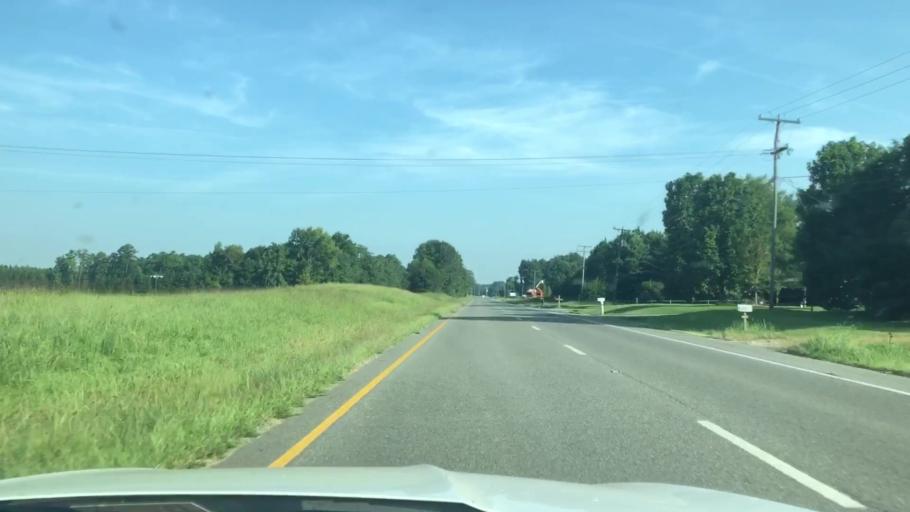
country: US
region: Virginia
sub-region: Middlesex County
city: Saluda
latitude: 37.7064
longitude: -76.6897
